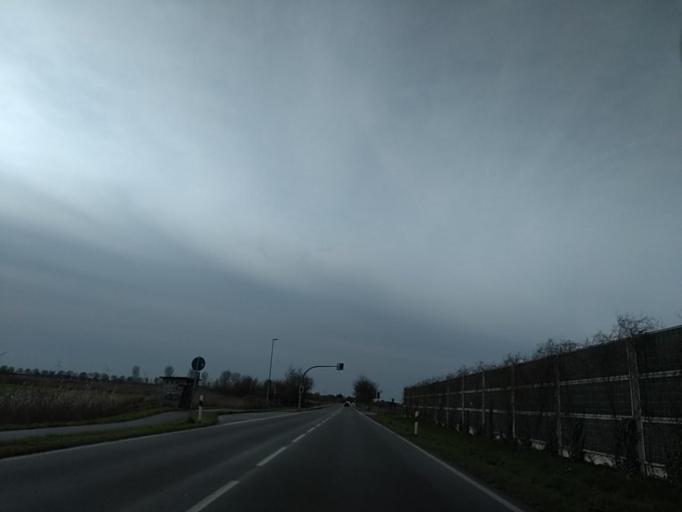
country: DE
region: Lower Saxony
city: Emden
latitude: 53.3606
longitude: 7.1360
